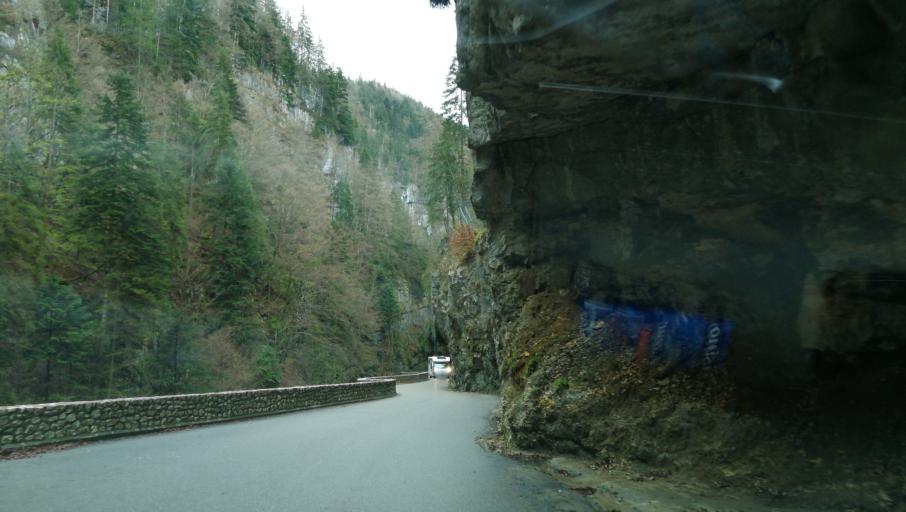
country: FR
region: Rhone-Alpes
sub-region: Departement de l'Isere
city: Villard-de-Lans
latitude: 45.0736
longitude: 5.5204
